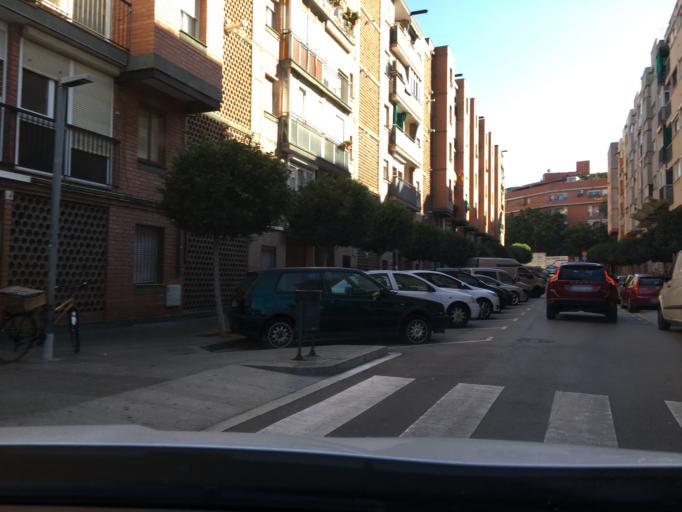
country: ES
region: Catalonia
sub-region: Provincia de Barcelona
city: Sant Feliu de Llobregat
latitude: 41.3848
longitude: 2.0399
